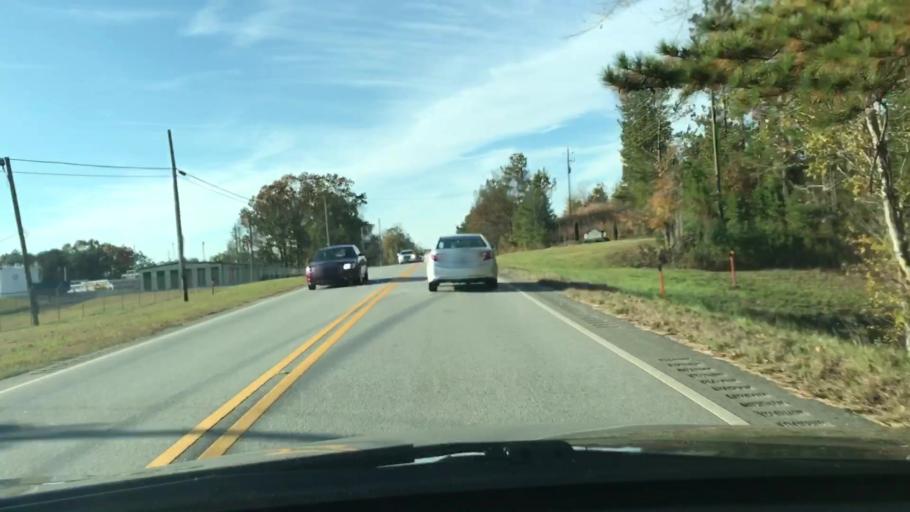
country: US
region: Alabama
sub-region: Cleburne County
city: Heflin
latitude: 33.6483
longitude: -85.5121
